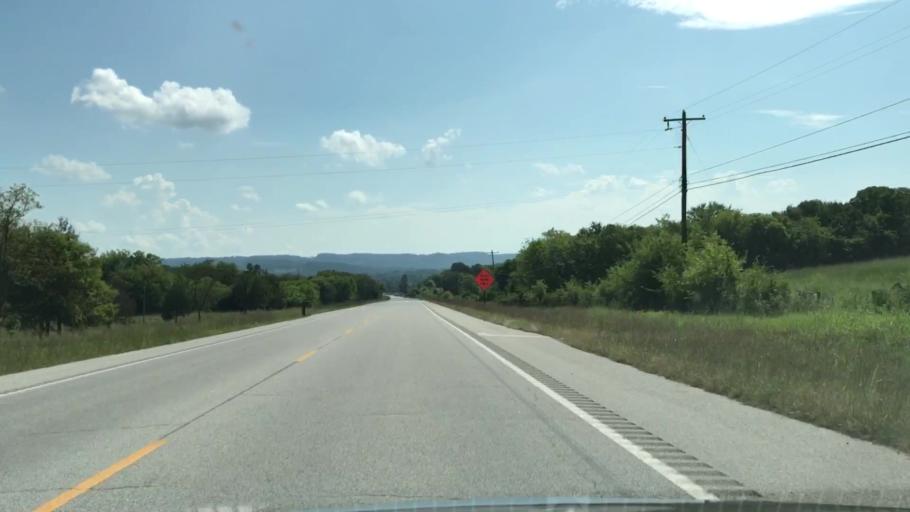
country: US
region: Tennessee
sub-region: Trousdale County
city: Hartsville
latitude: 36.3676
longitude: -86.0876
